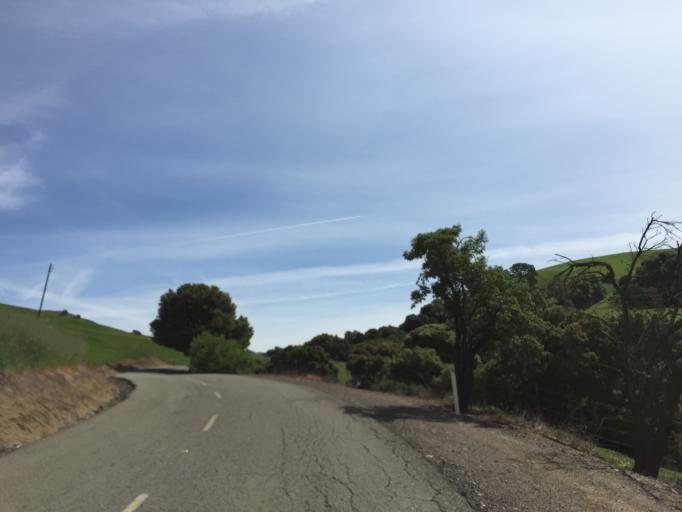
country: US
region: California
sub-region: Contra Costa County
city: Alamo
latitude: 37.8938
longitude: -121.9871
